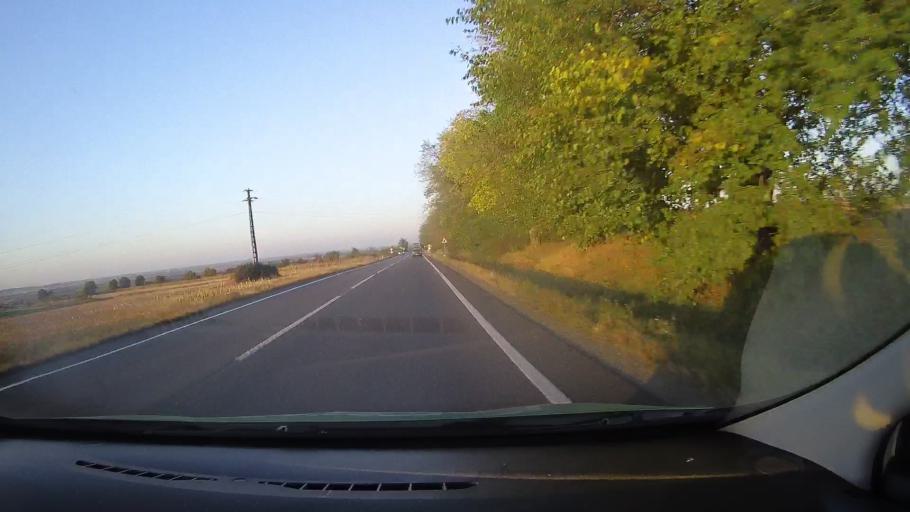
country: RO
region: Bihor
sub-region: Comuna Rosiori
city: Rosiori
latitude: 47.2726
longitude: 21.9771
